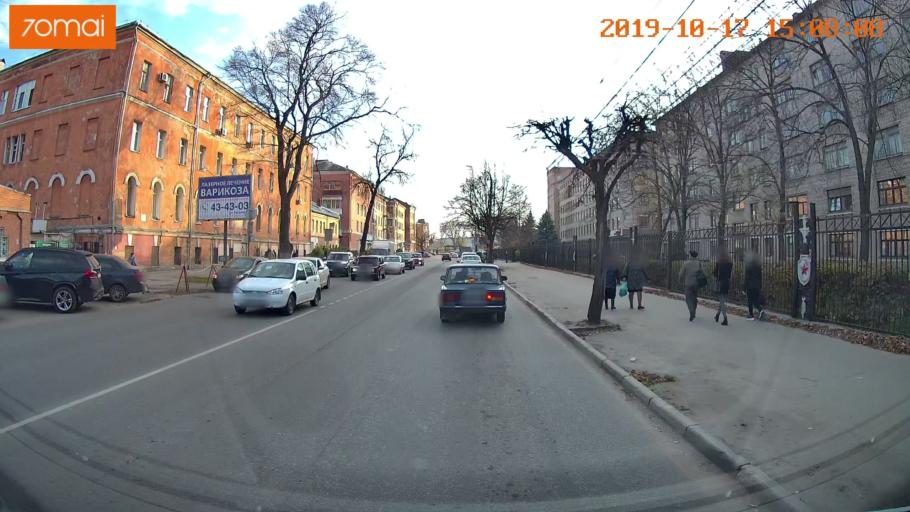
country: RU
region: Rjazan
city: Ryazan'
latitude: 54.6315
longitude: 39.7241
